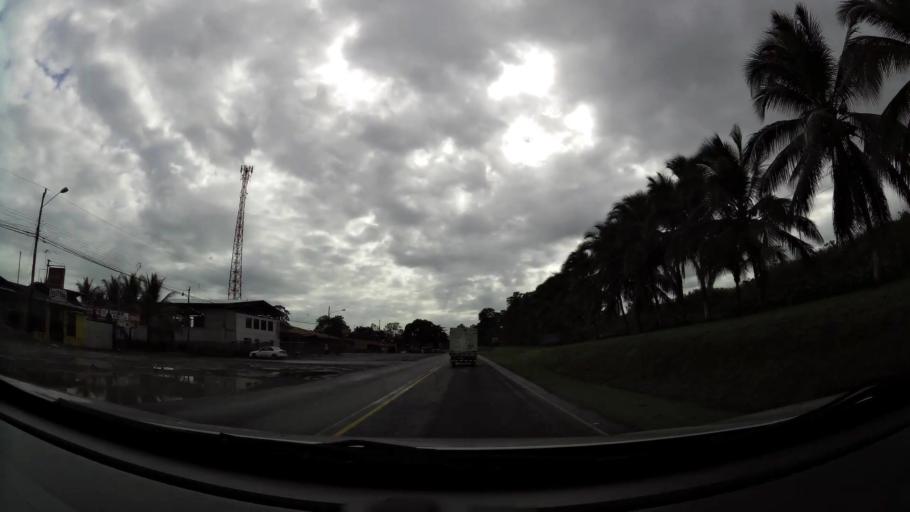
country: CR
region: Limon
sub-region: Canton de Siquirres
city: Siquirres
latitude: 10.1154
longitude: -83.5432
